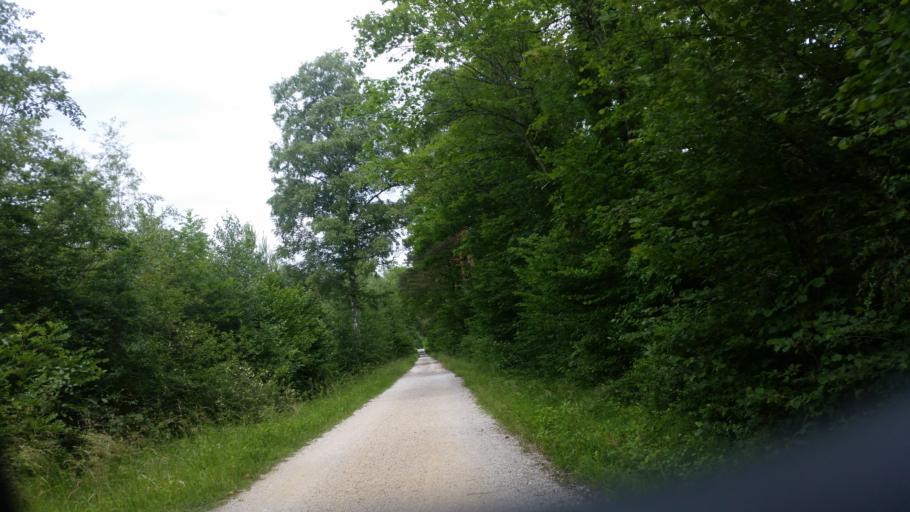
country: CH
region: Vaud
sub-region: Jura-Nord vaudois District
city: Yvonand
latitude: 46.8014
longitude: 6.7615
